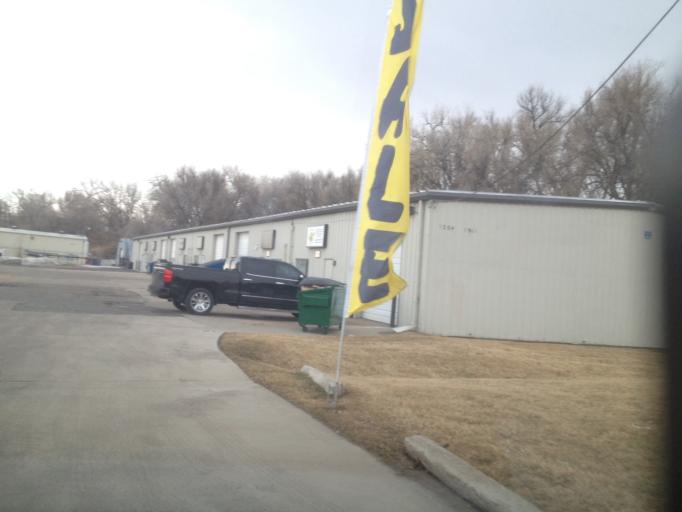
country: US
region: Colorado
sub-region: Adams County
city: Berkley
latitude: 39.7943
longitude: -105.0438
